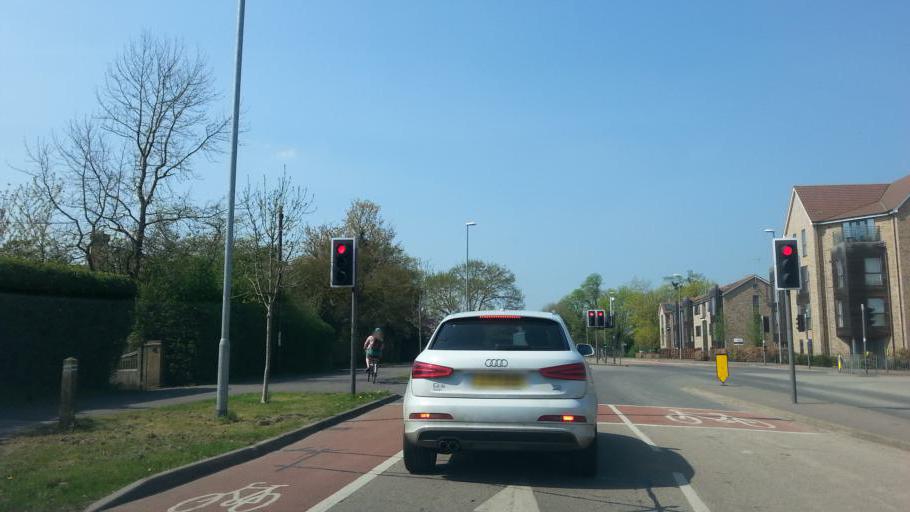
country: GB
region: England
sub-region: Cambridgeshire
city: Girton
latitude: 52.2217
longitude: 0.0956
